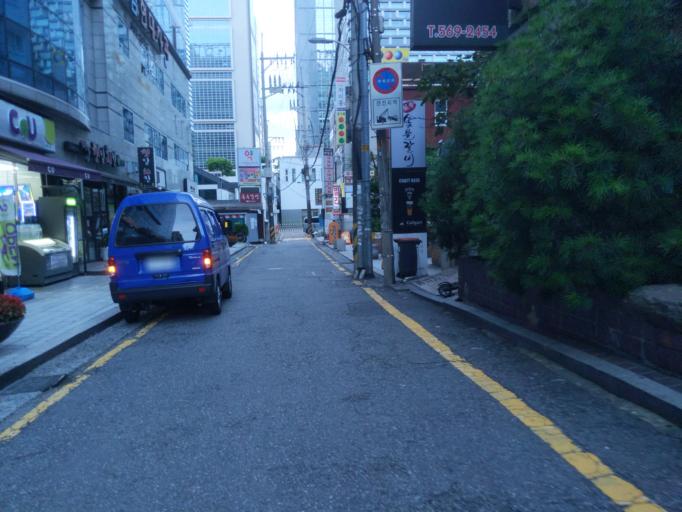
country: KR
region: Seoul
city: Seoul
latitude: 37.5088
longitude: 127.0581
